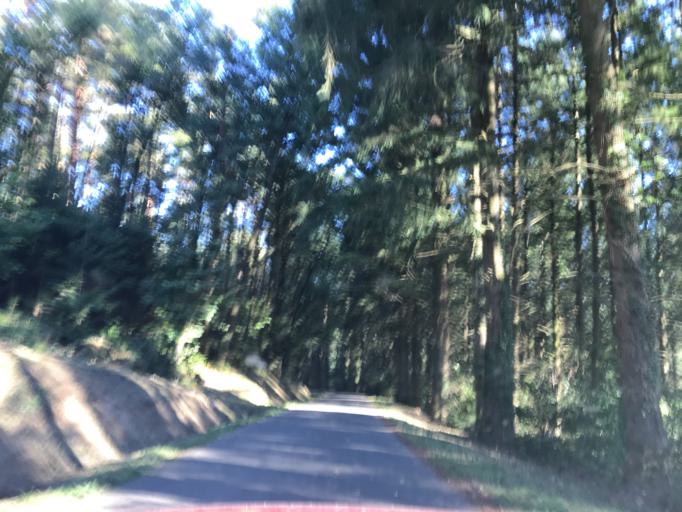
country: FR
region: Auvergne
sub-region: Departement du Puy-de-Dome
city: Escoutoux
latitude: 45.7665
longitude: 3.6297
